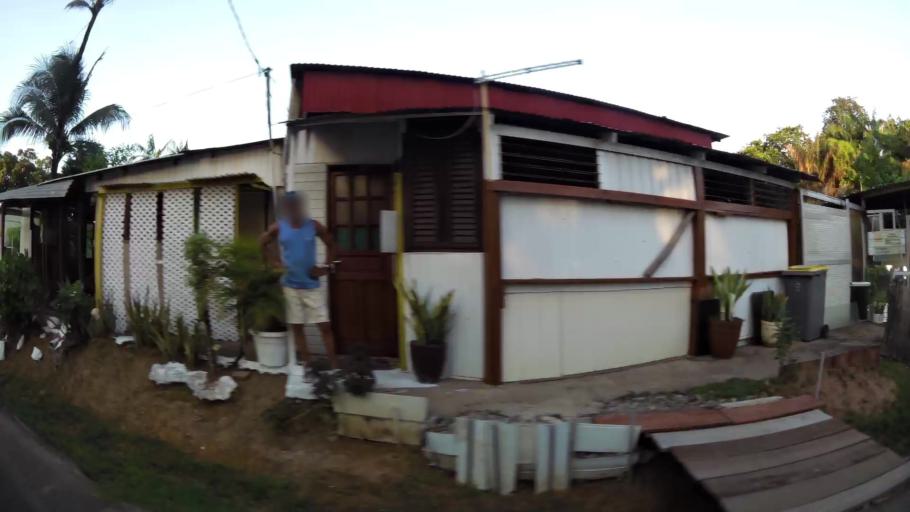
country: GF
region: Guyane
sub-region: Guyane
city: Cayenne
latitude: 4.9291
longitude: -52.3042
